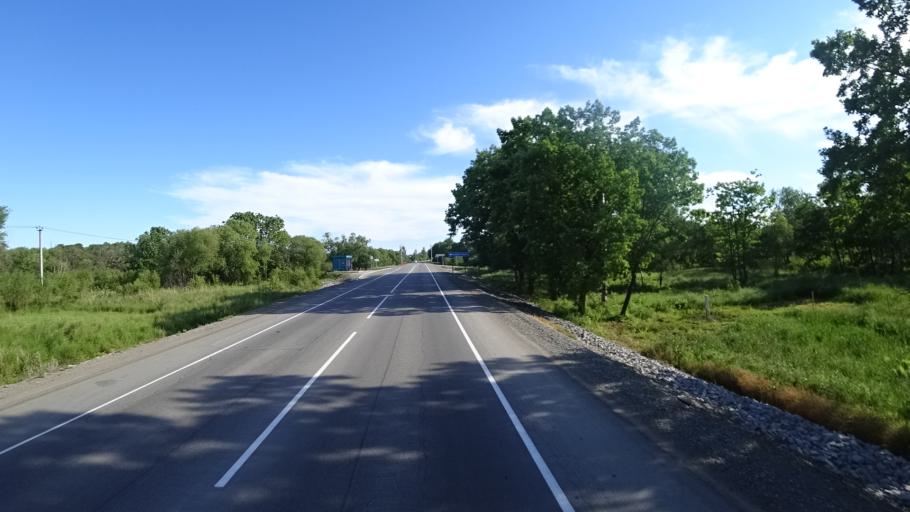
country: RU
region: Khabarovsk Krai
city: Khor
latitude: 47.8579
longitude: 134.9624
